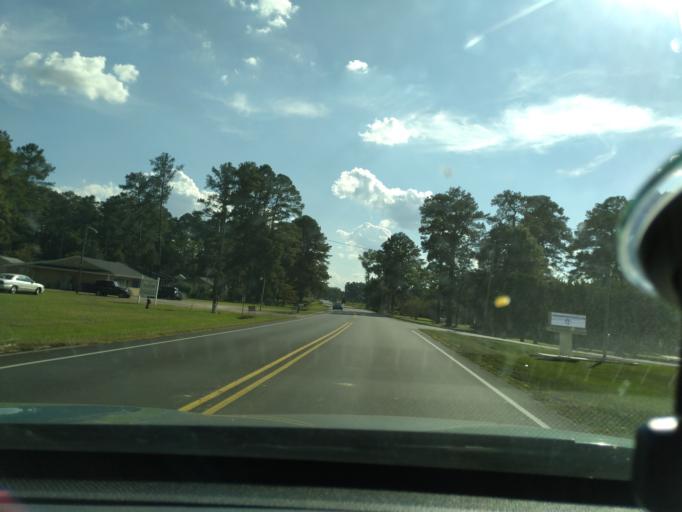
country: US
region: North Carolina
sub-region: Nash County
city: Sharpsburg
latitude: 35.9035
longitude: -77.8502
